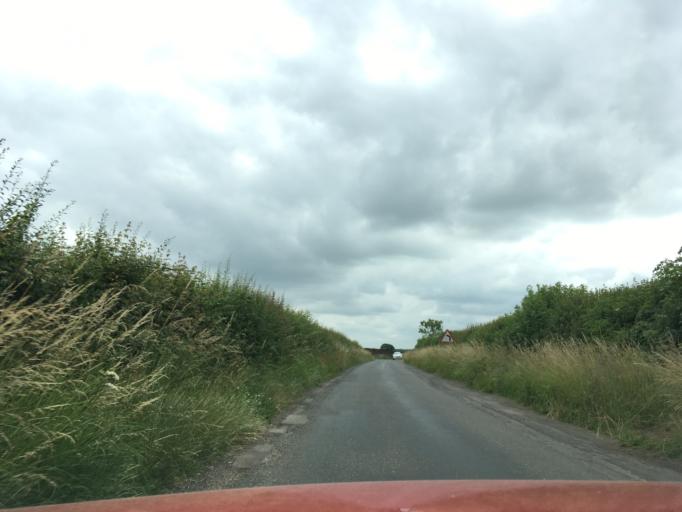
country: GB
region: England
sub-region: Oxfordshire
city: Charlbury
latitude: 51.9168
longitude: -1.4850
